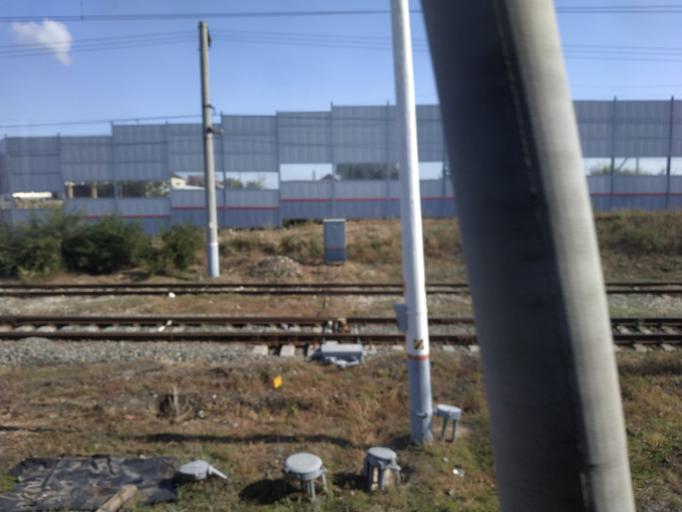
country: RU
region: Volgograd
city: Gumrak
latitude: 48.7760
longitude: 44.3812
